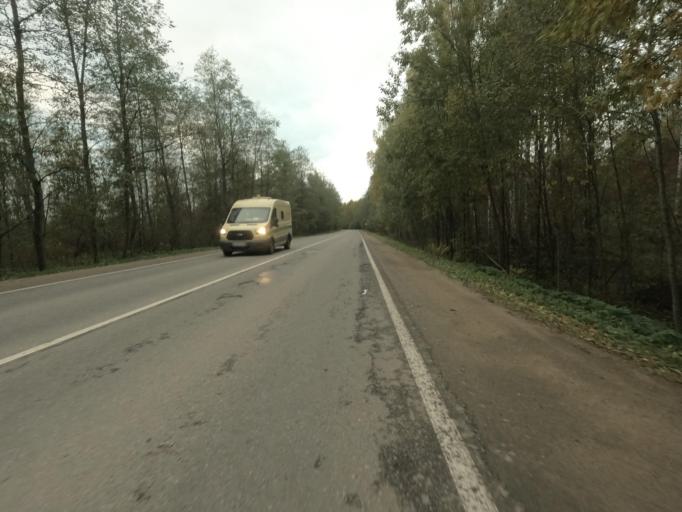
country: RU
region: Leningrad
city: Pavlovo
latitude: 59.7993
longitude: 30.9433
